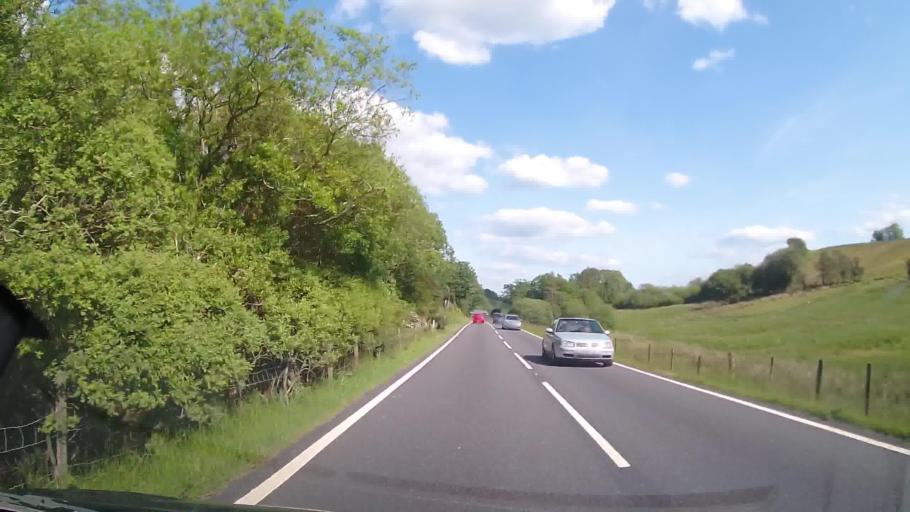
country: GB
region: Wales
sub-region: Gwynedd
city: Bala
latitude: 52.7108
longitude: -3.5699
